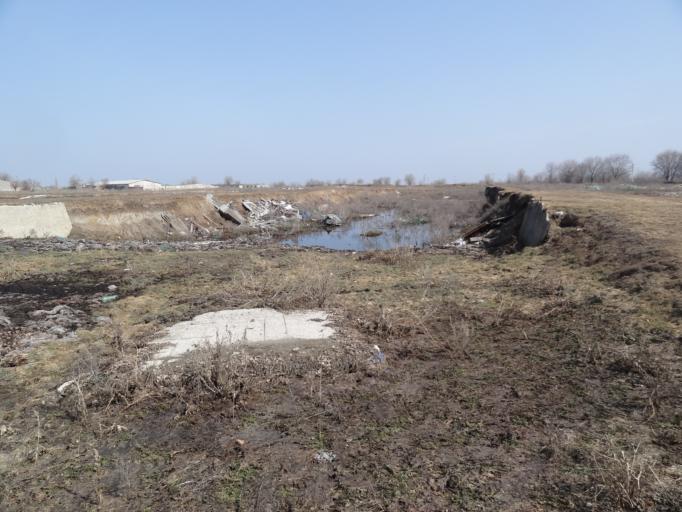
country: RU
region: Saratov
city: Engel's
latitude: 51.4217
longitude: 46.1841
